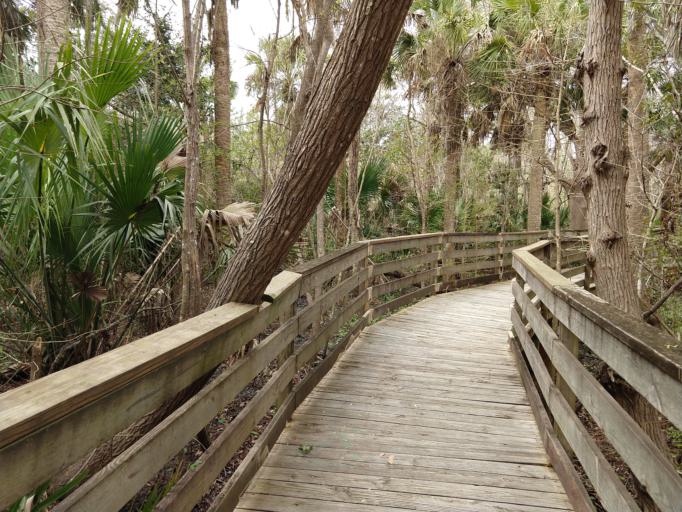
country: US
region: Florida
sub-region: Franklin County
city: Apalachicola
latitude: 29.7328
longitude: -84.9971
